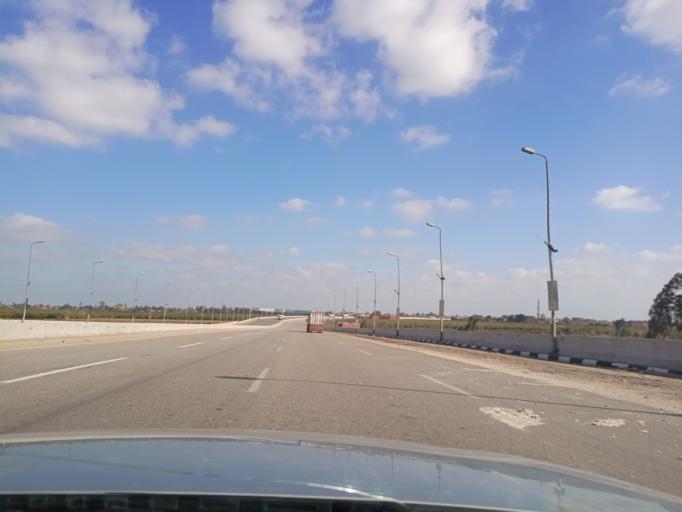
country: EG
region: Muhafazat al Minufiyah
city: Ashmun
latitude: 30.3279
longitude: 30.8341
